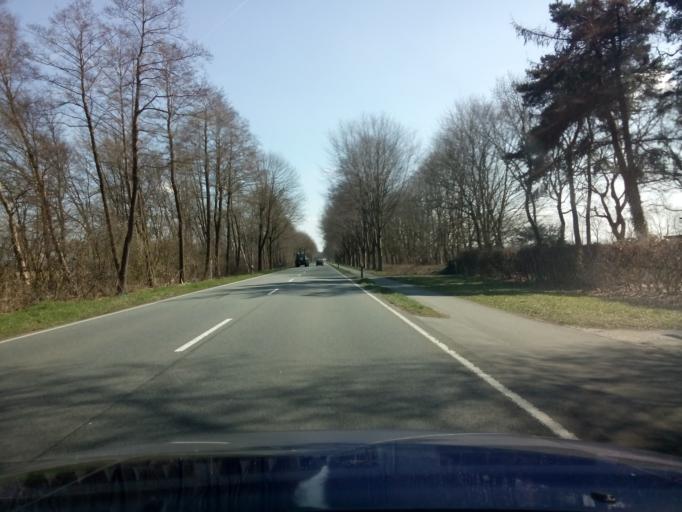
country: DE
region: Lower Saxony
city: Laar
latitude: 52.6274
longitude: 6.7789
